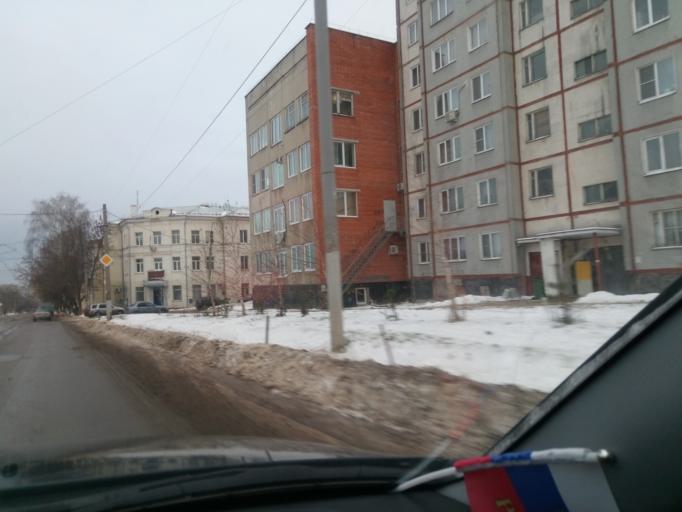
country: RU
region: Tula
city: Tula
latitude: 54.1757
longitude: 37.6220
